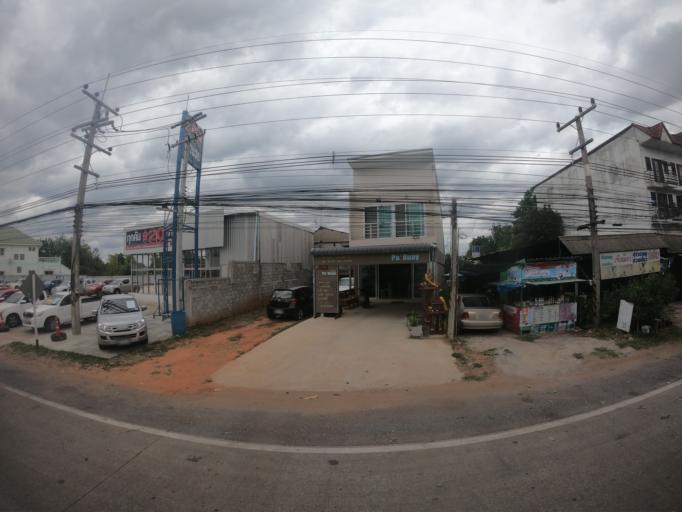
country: TH
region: Nakhon Ratchasima
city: Nakhon Ratchasima
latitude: 14.9079
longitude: 102.1544
